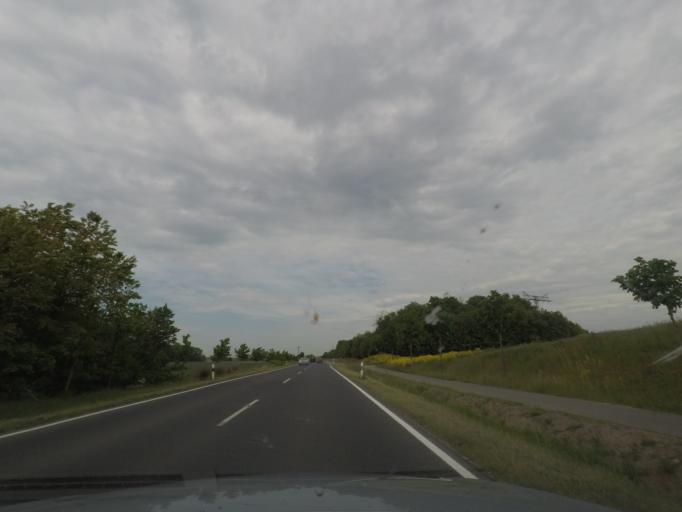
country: DE
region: Brandenburg
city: Grunow
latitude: 53.3380
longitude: 13.9308
